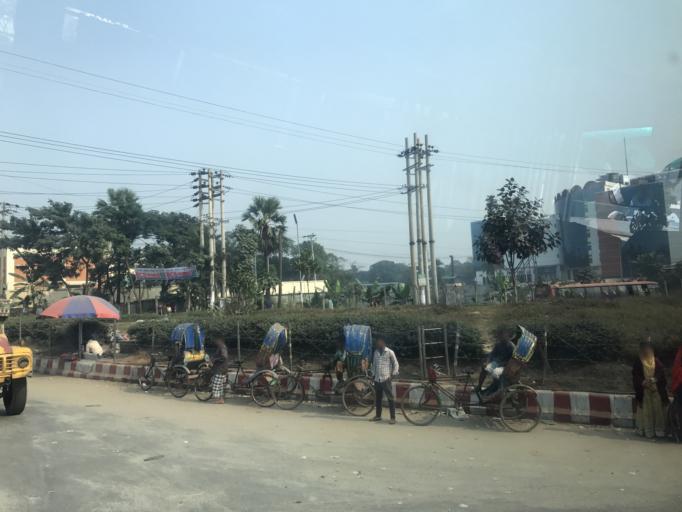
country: BD
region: Dhaka
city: Tungi
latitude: 23.9135
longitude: 90.2584
